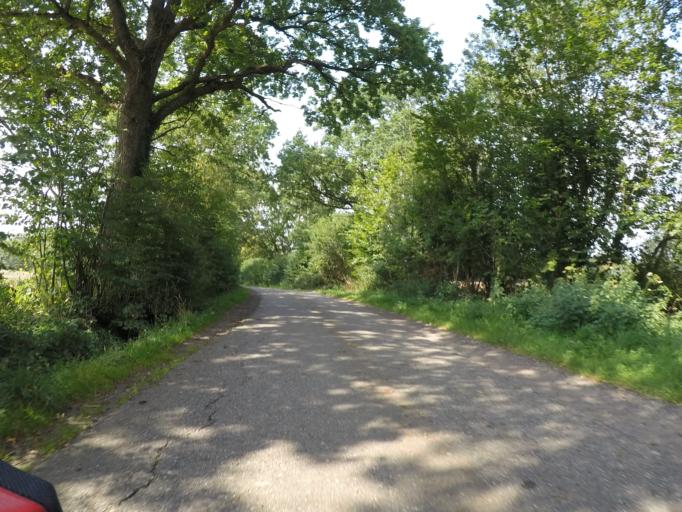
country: DE
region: Schleswig-Holstein
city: Kisdorf
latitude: 53.7768
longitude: 10.0382
